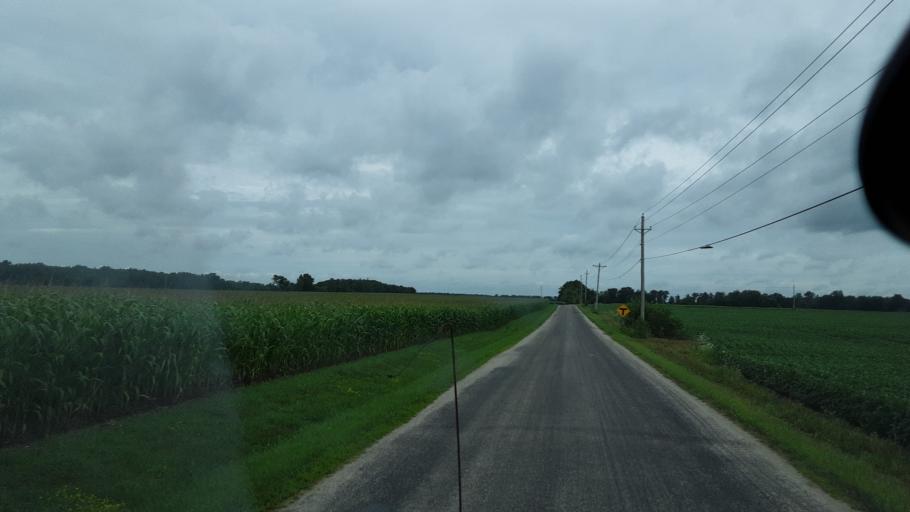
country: US
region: Indiana
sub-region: Adams County
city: Geneva
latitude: 40.5302
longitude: -85.0104
